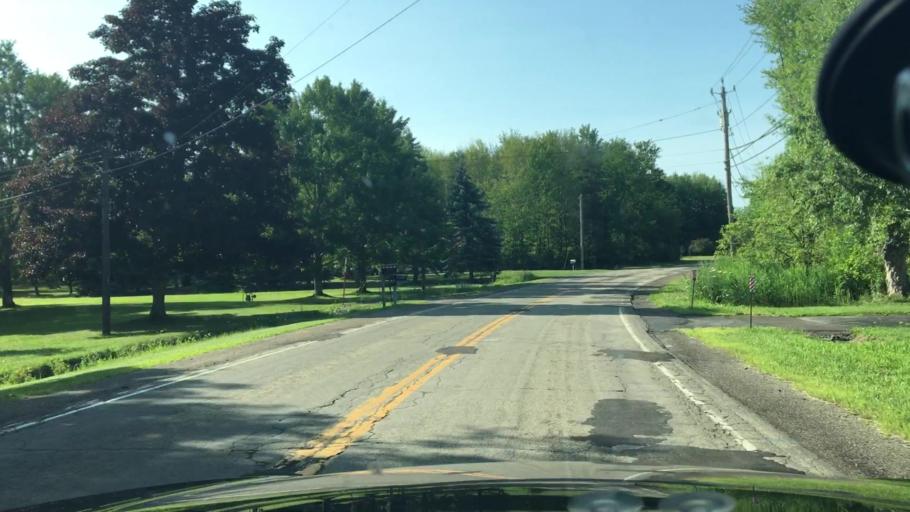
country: US
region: New York
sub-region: Erie County
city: Angola
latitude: 42.6253
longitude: -79.0260
